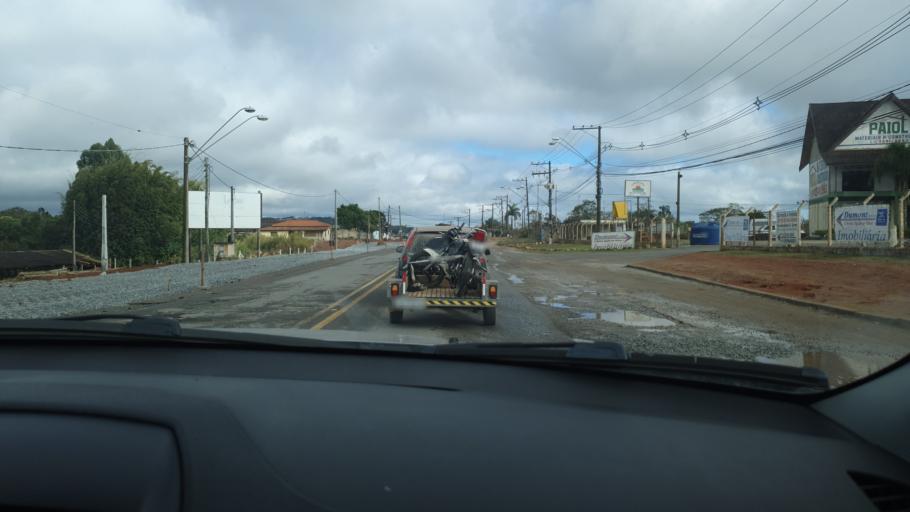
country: BR
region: Sao Paulo
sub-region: Ibiuna
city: Ibiuna
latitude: -23.6572
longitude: -47.1994
